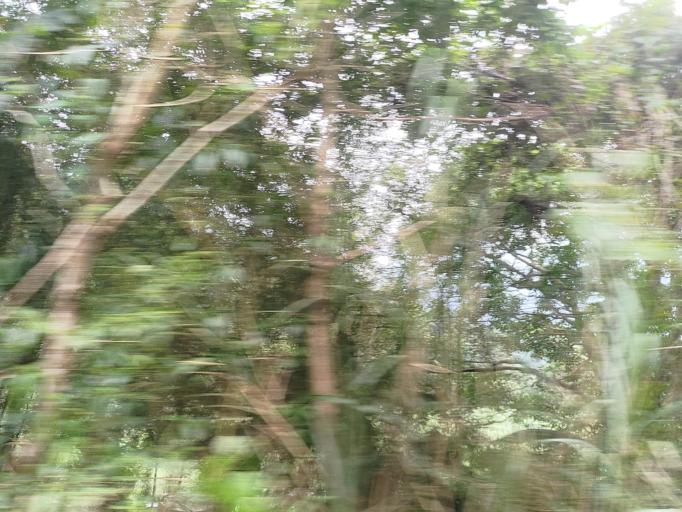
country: TW
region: Taiwan
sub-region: Hsinchu
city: Hsinchu
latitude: 24.6235
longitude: 121.0900
